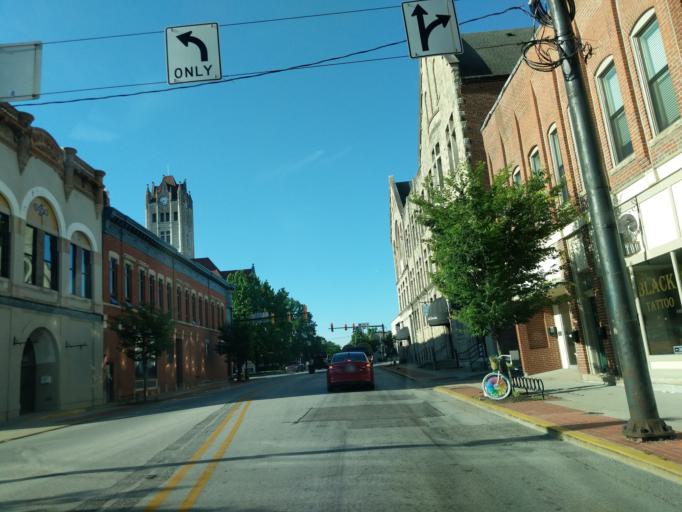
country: US
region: Indiana
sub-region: Hancock County
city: Greenfield
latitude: 39.7860
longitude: -85.7694
